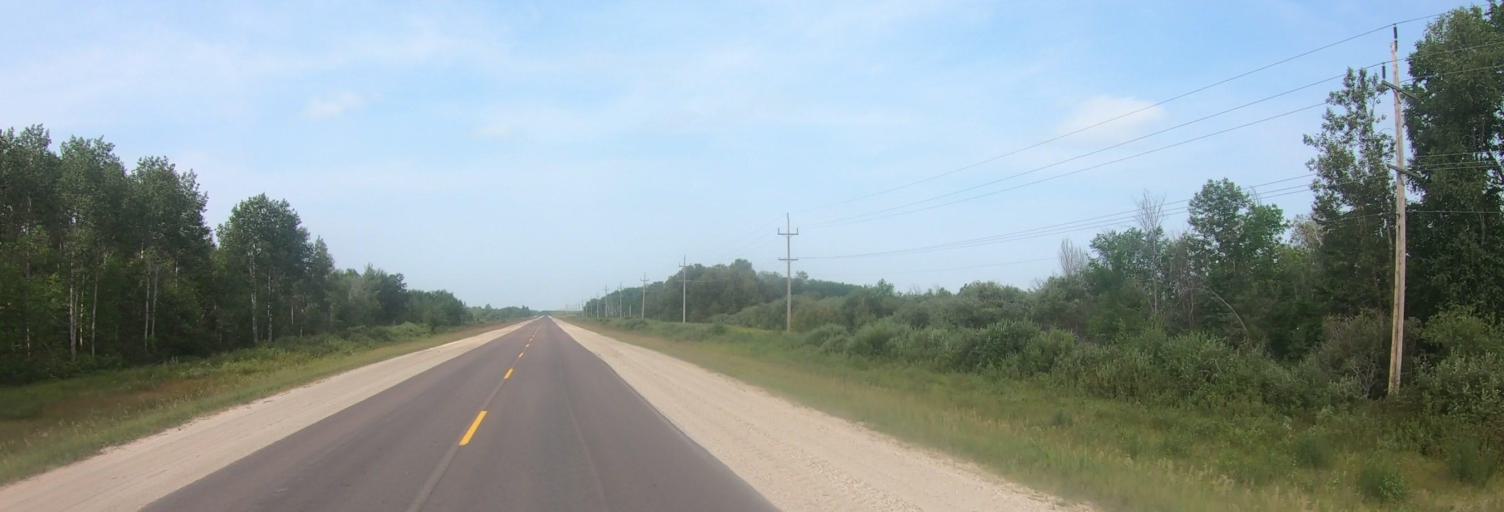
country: CA
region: Manitoba
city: La Broquerie
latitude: 49.2669
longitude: -96.4495
